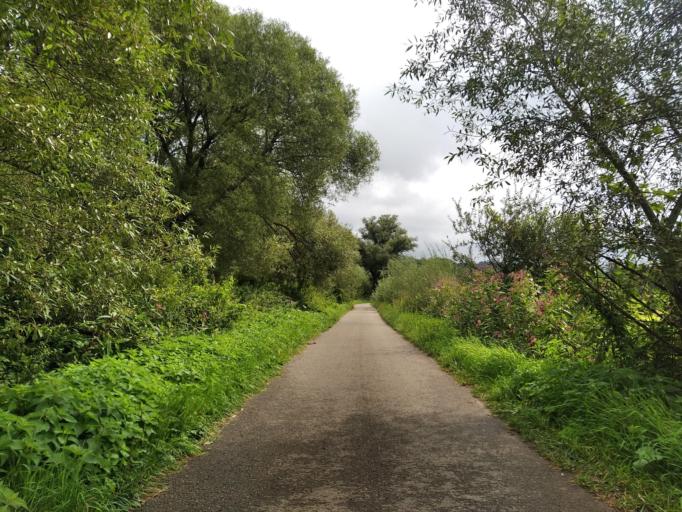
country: PL
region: Subcarpathian Voivodeship
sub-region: Powiat brzozowski
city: Nozdrzec
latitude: 49.7471
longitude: 22.2282
